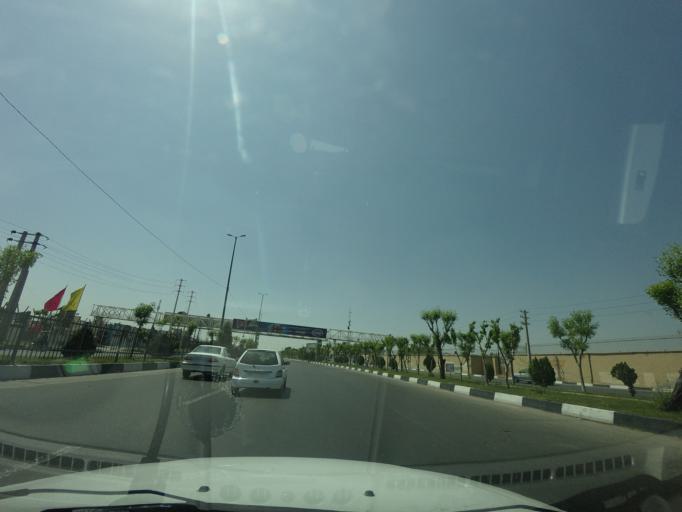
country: IR
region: Tehran
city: Eslamshahr
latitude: 35.5782
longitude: 51.2669
